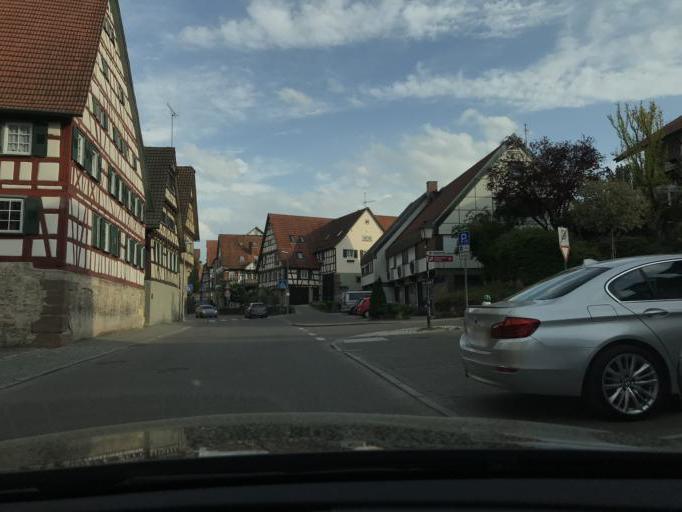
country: DE
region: Baden-Wuerttemberg
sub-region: Regierungsbezirk Stuttgart
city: Weinstadt-Endersbach
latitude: 48.7822
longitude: 9.3665
